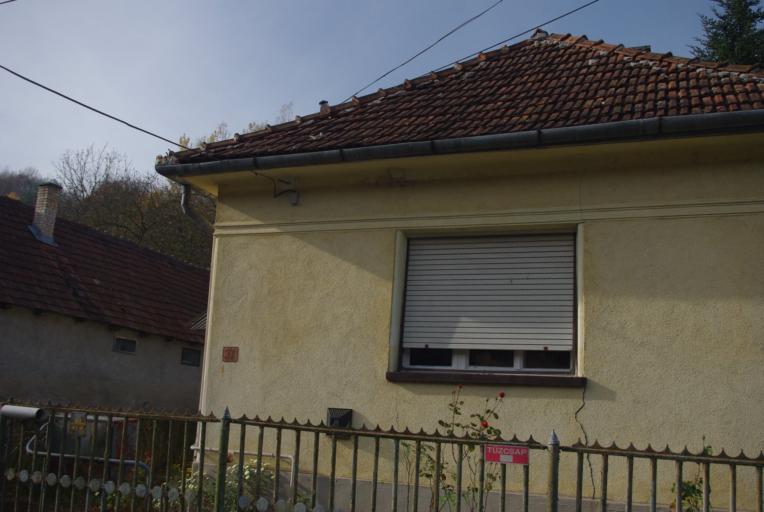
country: HU
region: Borsod-Abauj-Zemplen
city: Sarospatak
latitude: 48.4294
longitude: 21.4930
